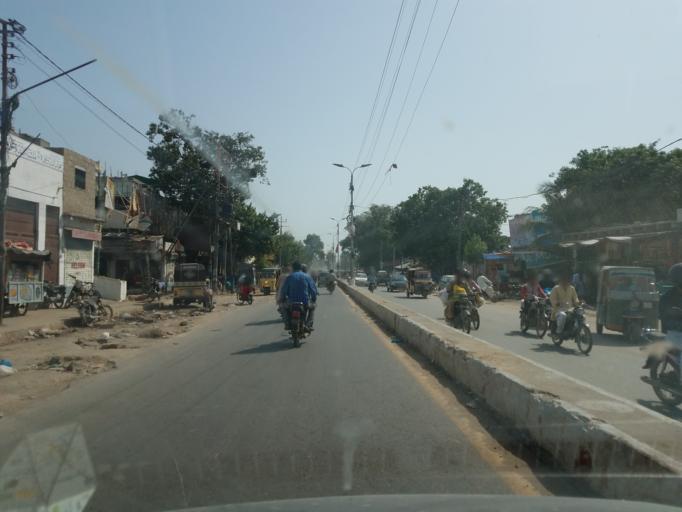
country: PK
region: Sindh
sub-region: Karachi District
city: Karachi
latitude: 24.8909
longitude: 67.0431
